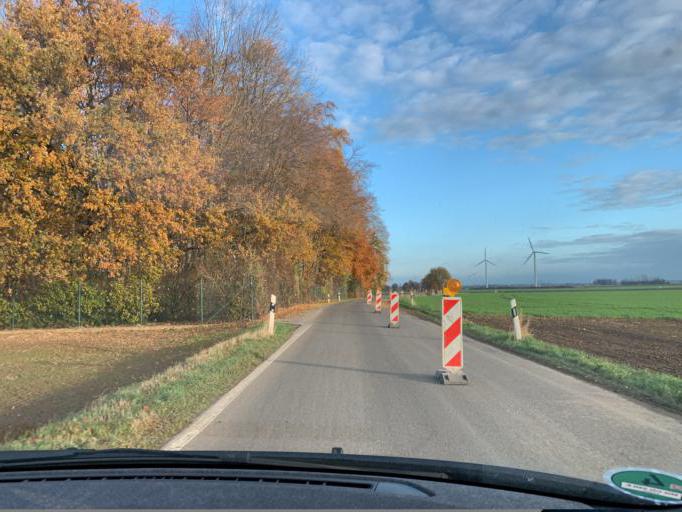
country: DE
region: North Rhine-Westphalia
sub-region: Regierungsbezirk Koln
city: Titz
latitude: 51.0553
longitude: 6.4048
